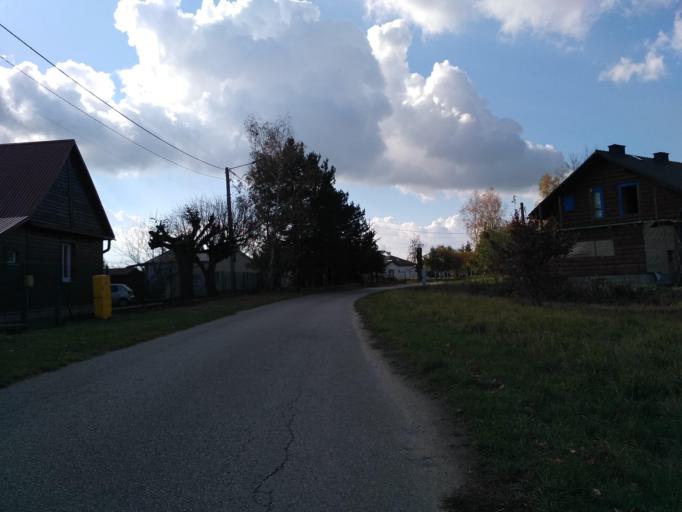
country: PL
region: Subcarpathian Voivodeship
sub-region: Powiat rzeszowski
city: Swilcza
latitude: 50.1212
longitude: 21.9037
